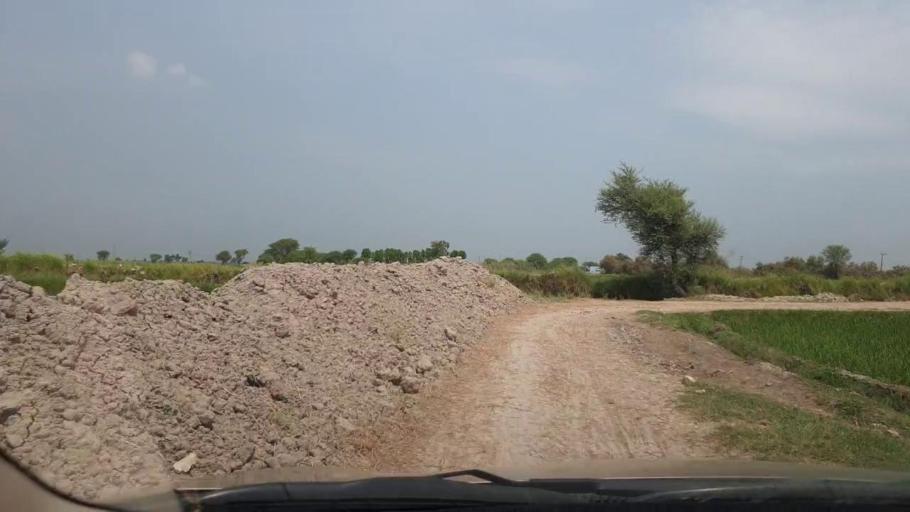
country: PK
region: Sindh
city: Goth Garelo
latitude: 27.5211
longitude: 68.1214
